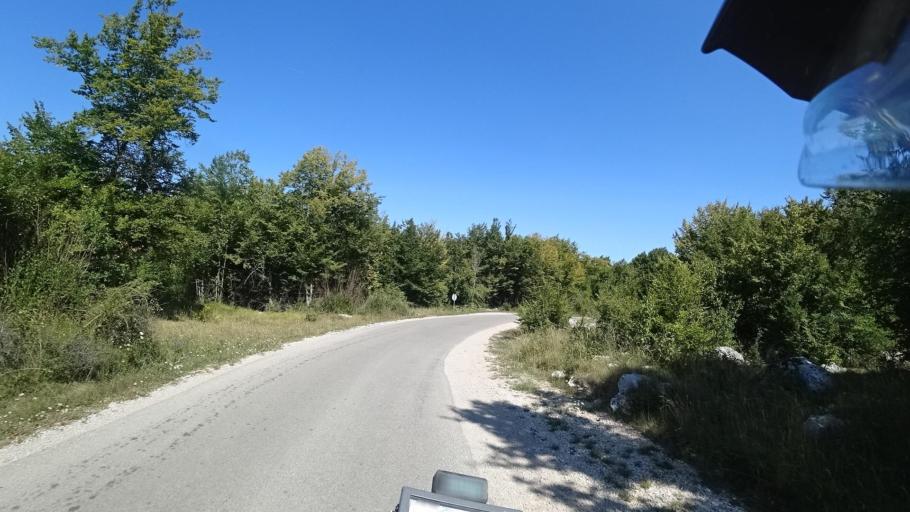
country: HR
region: Licko-Senjska
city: Popovaca
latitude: 44.7298
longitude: 15.2932
